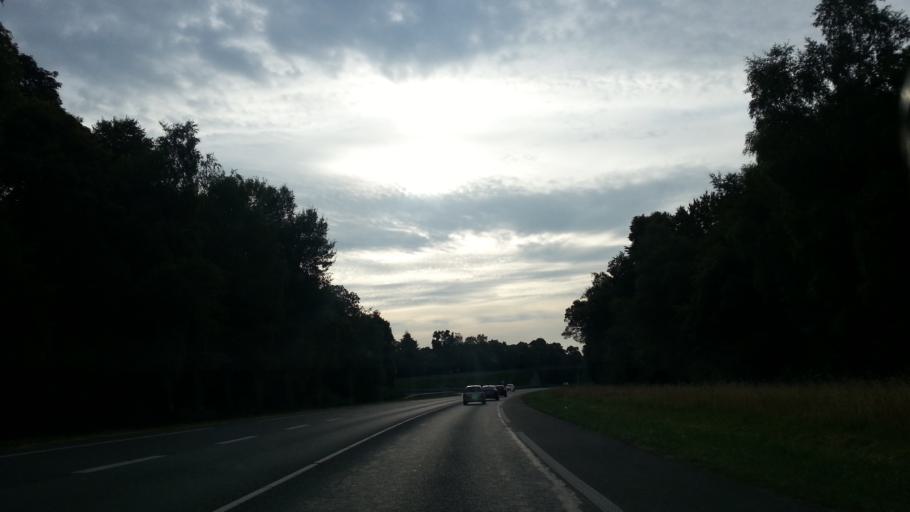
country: FR
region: Picardie
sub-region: Departement de l'Oise
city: Creil
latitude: 49.2426
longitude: 2.5055
